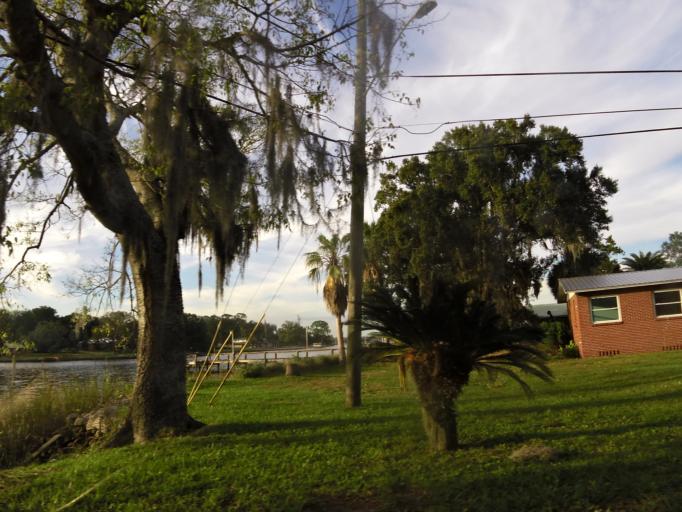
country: US
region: Florida
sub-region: Duval County
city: Jacksonville
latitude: 30.3916
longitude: -81.6609
